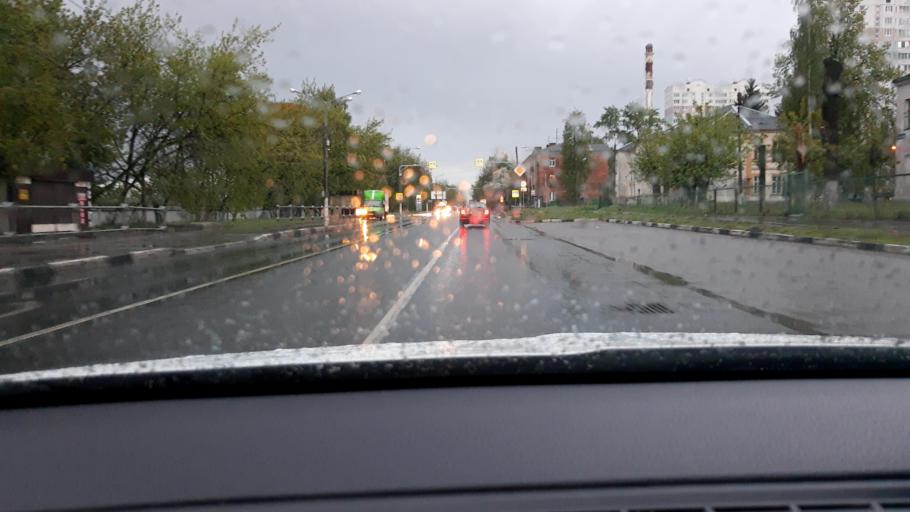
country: RU
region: Moskovskaya
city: Zagoryanskiy
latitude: 55.9267
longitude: 37.9590
